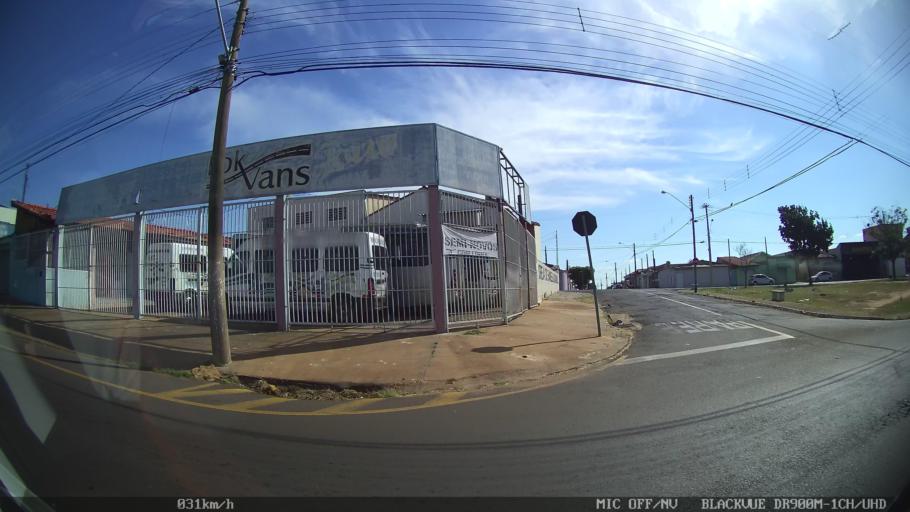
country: BR
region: Sao Paulo
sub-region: Franca
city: Franca
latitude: -20.5015
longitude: -47.3990
